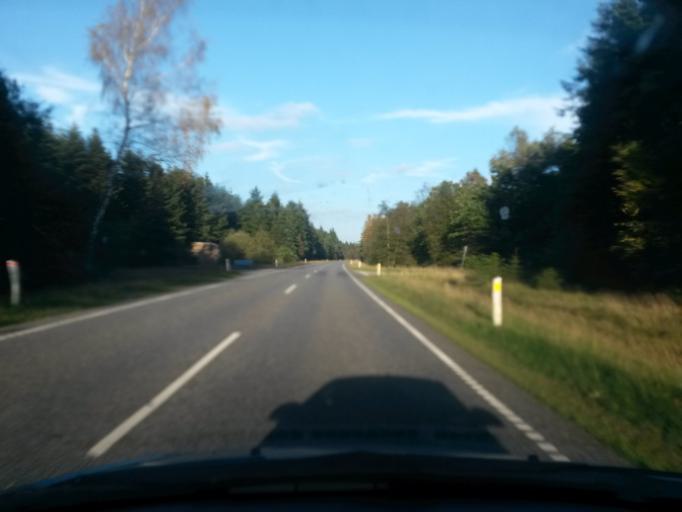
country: DK
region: Central Jutland
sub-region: Herning Kommune
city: Sunds
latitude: 56.3273
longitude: 8.9446
